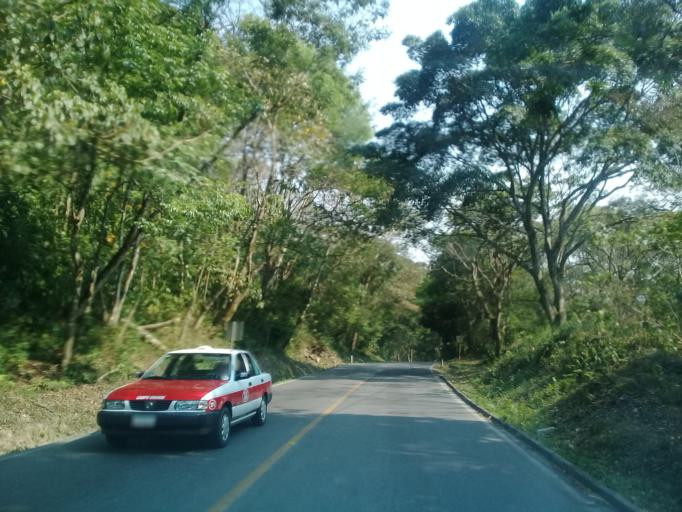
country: MX
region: Veracruz
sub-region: Ixtaczoquitlan
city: Campo Chico
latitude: 18.8444
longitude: -97.0301
